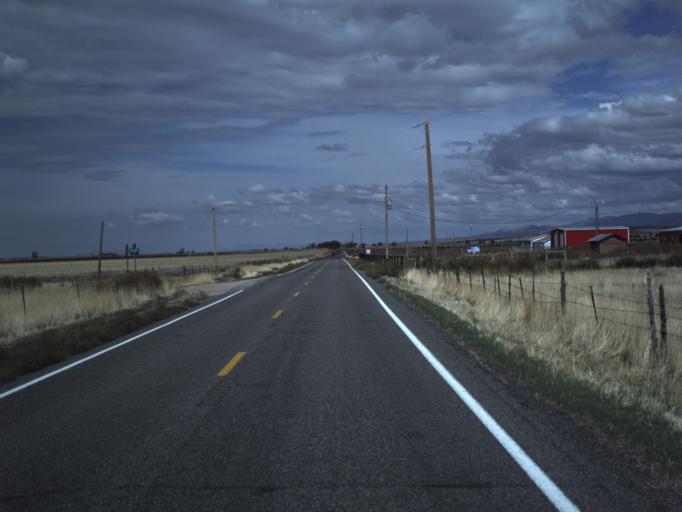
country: US
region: Utah
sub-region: Millard County
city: Fillmore
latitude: 39.0227
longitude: -112.4100
